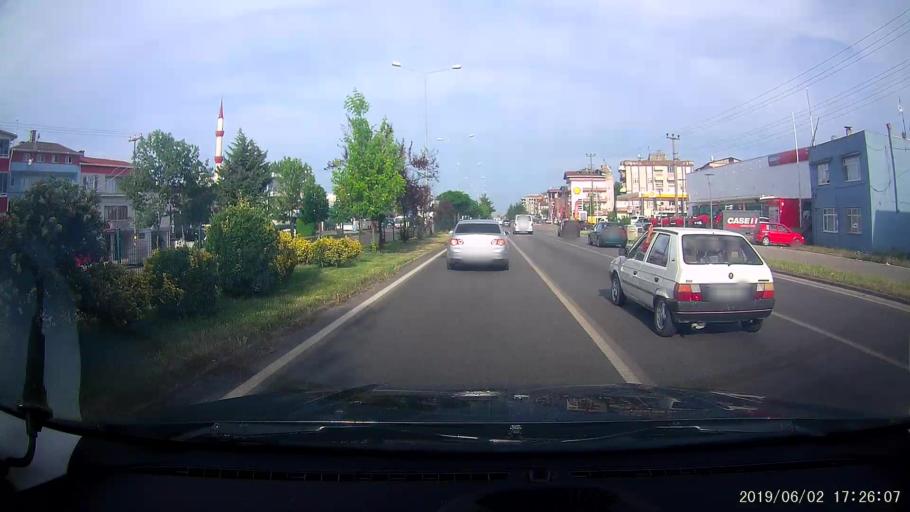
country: TR
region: Samsun
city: Carsamba
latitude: 41.2044
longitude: 36.7162
